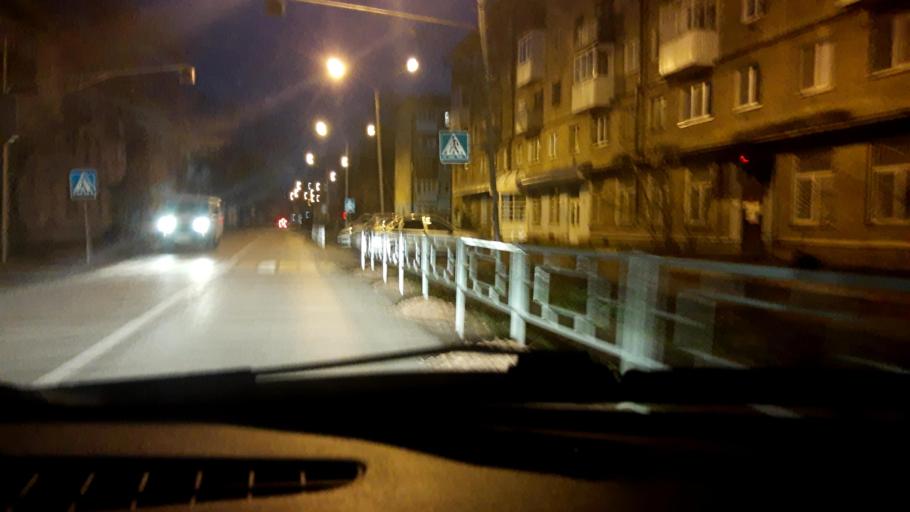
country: RU
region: Bashkortostan
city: Mikhaylovka
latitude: 54.7060
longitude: 55.8383
